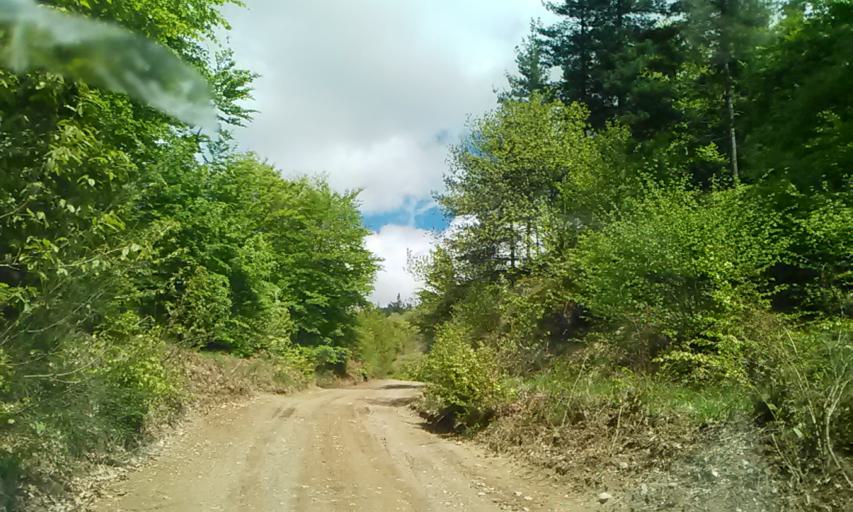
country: IT
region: Piedmont
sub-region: Provincia di Vercelli
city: Civiasco
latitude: 45.7941
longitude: 8.3043
